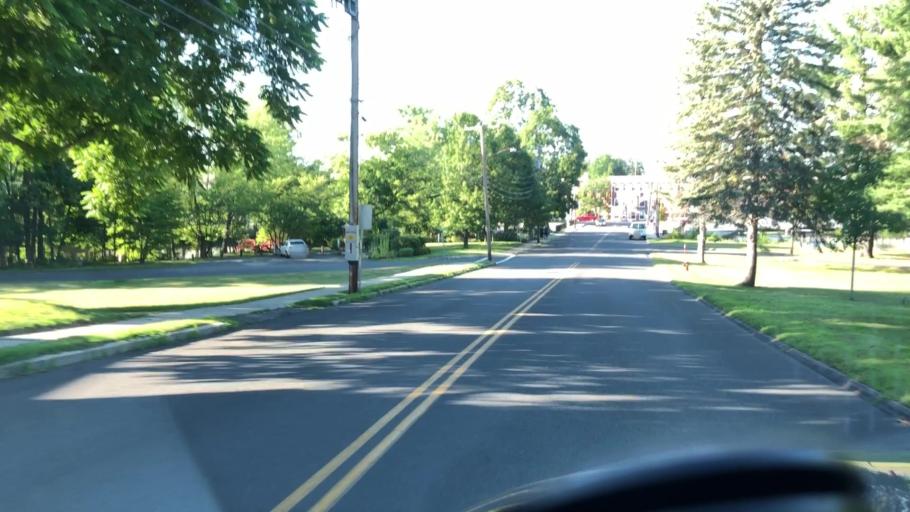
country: US
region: Massachusetts
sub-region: Hampshire County
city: Easthampton
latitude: 42.2638
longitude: -72.6698
